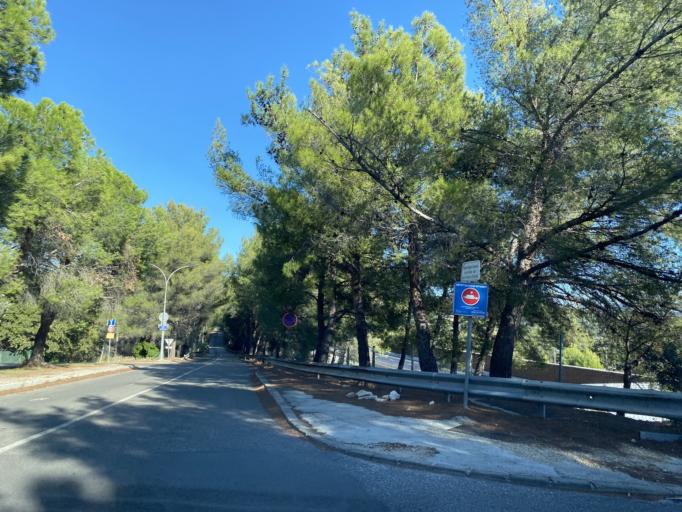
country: FR
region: Provence-Alpes-Cote d'Azur
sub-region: Departement des Bouches-du-Rhone
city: Ceyreste
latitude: 43.2059
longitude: 5.6097
